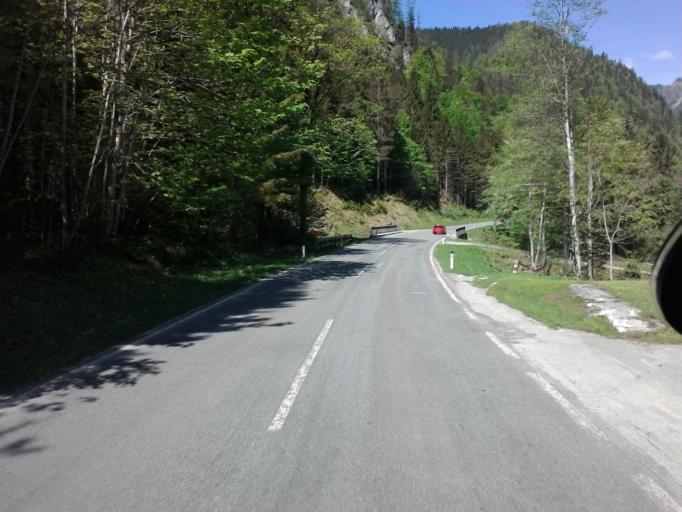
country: AT
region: Styria
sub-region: Politischer Bezirk Liezen
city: Wildalpen
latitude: 47.6735
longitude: 14.9341
